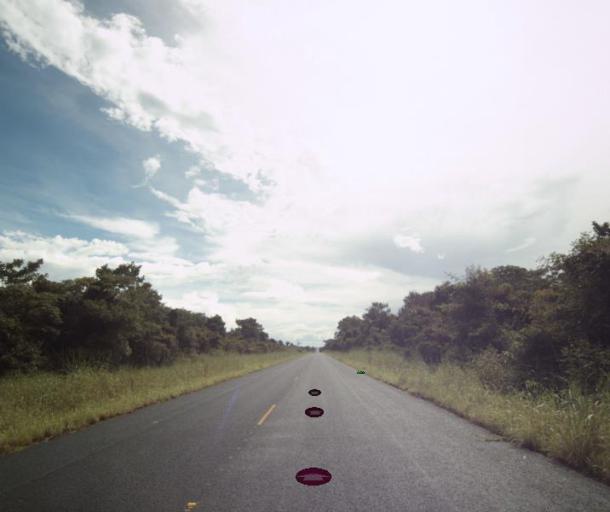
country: BR
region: Goias
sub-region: Sao Miguel Do Araguaia
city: Sao Miguel do Araguaia
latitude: -13.2996
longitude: -50.3107
